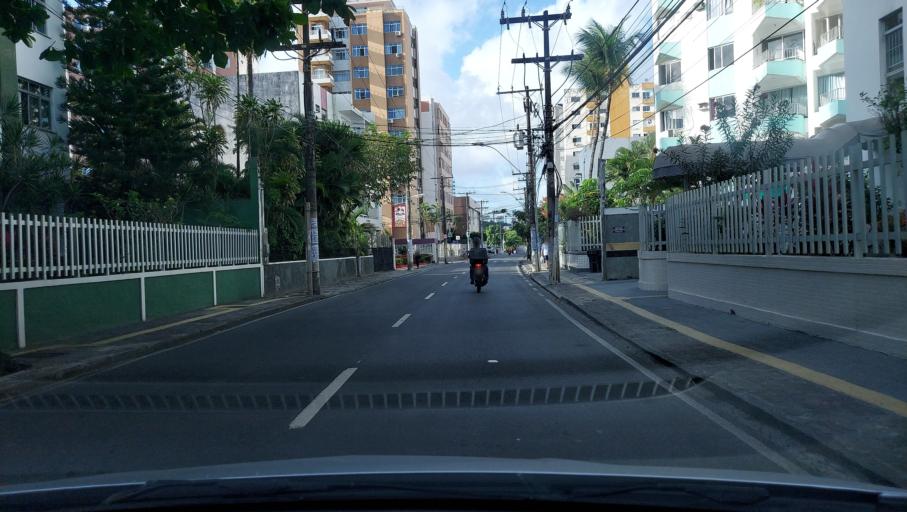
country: BR
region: Bahia
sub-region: Salvador
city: Salvador
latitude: -12.9944
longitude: -38.4480
